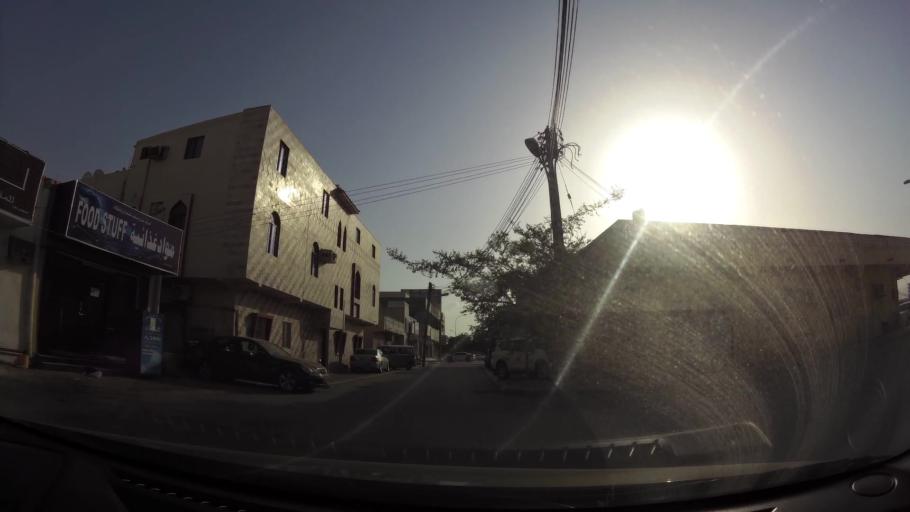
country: OM
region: Zufar
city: Salalah
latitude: 17.0116
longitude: 54.0909
